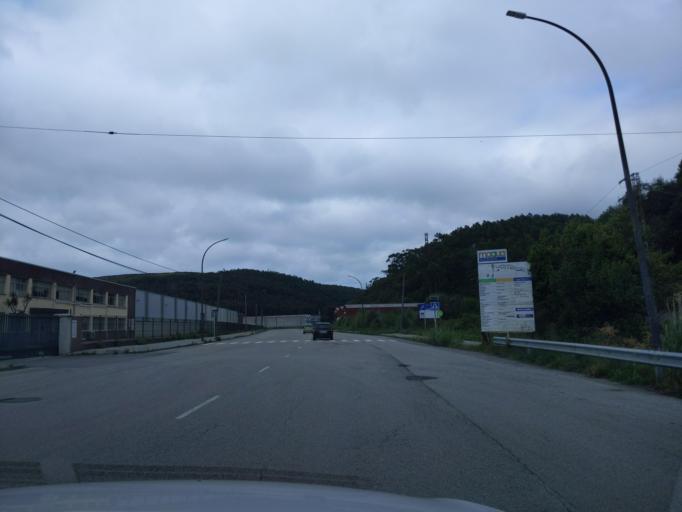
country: ES
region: Asturias
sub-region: Province of Asturias
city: Aviles
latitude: 43.5955
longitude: -5.9149
